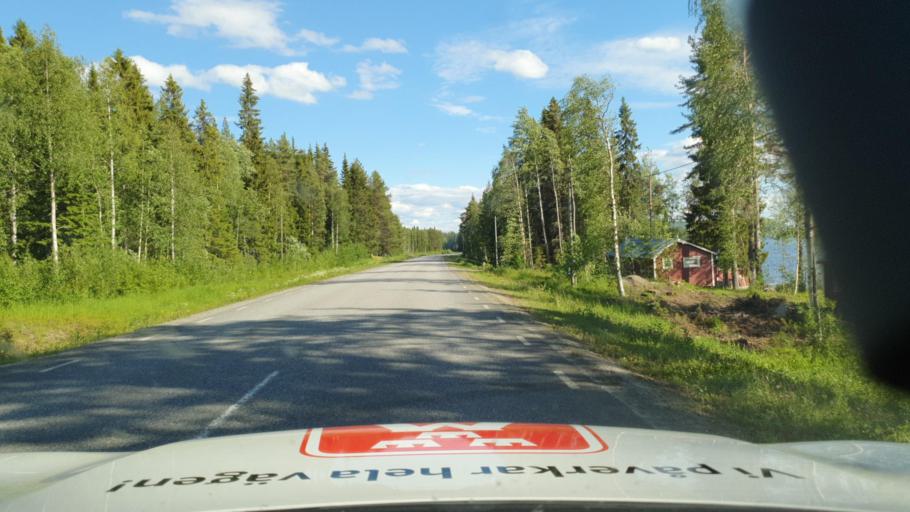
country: SE
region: Vaesterbotten
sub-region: Norsjo Kommun
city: Norsjoe
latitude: 64.8406
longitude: 19.7607
